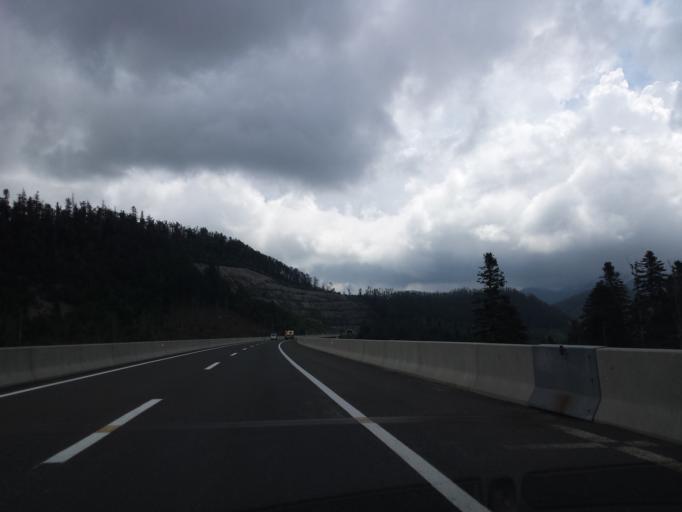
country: HR
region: Primorsko-Goranska
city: Hreljin
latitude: 45.3164
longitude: 14.7079
